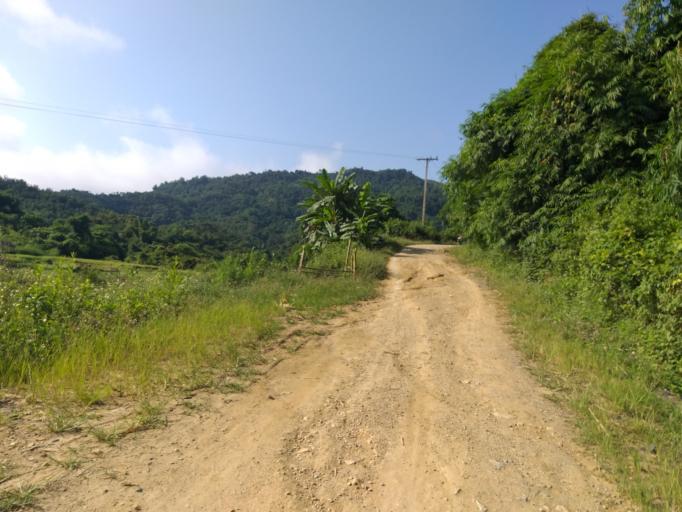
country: LA
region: Phongsali
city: Khoa
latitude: 21.2019
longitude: 102.6840
